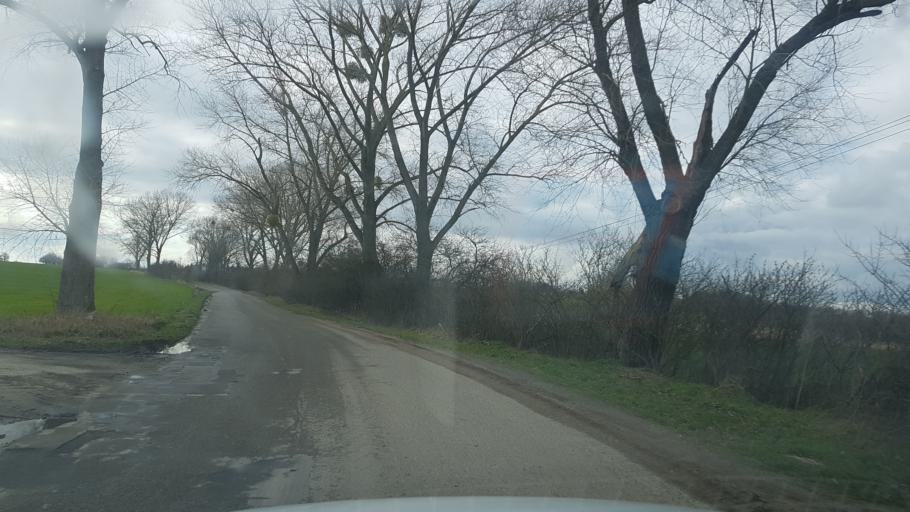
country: PL
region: West Pomeranian Voivodeship
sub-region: Powiat policki
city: Kolbaskowo
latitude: 53.3604
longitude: 14.4228
